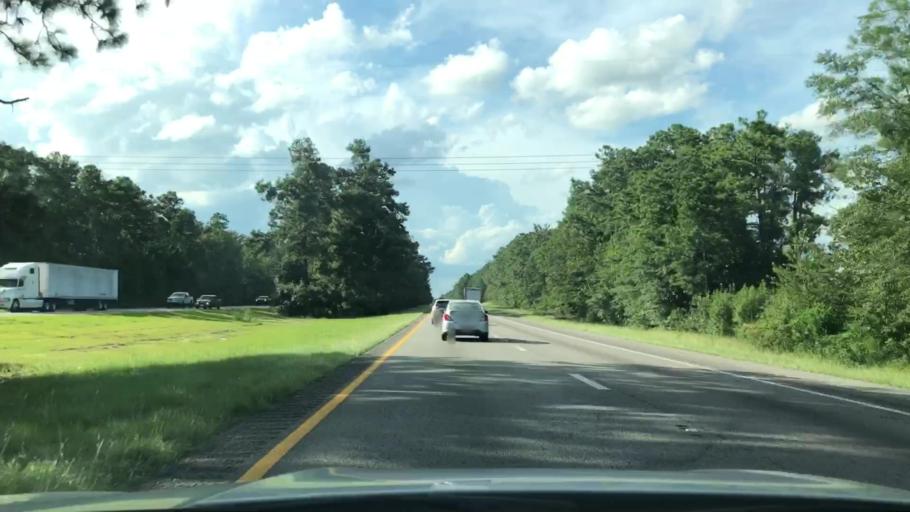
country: US
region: South Carolina
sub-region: Calhoun County
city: Saint Matthews
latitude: 33.6419
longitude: -80.8798
